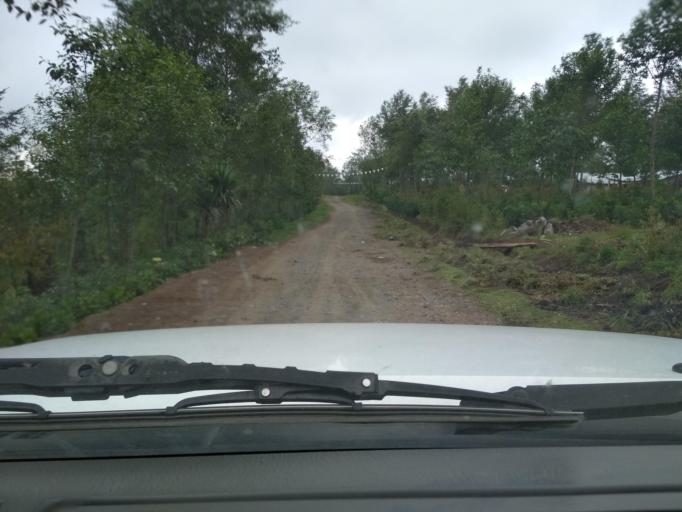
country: MX
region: Veracruz
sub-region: La Perla
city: Chilapa
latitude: 18.9922
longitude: -97.1642
